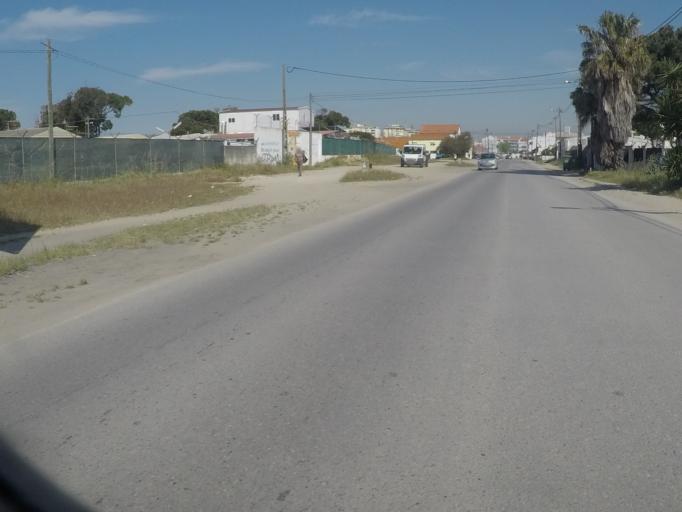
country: PT
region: Setubal
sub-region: Almada
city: Costa de Caparica
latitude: 38.6347
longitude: -9.2269
